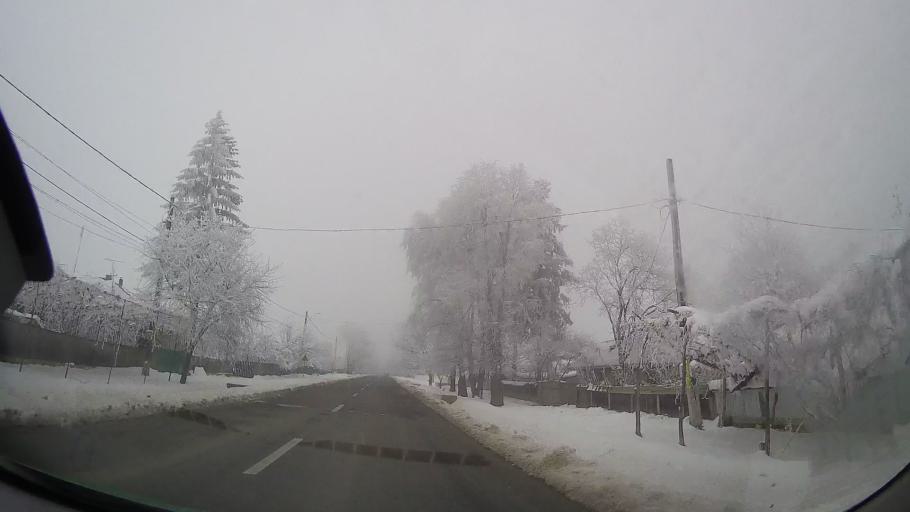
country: RO
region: Iasi
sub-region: Comuna Mogosesti-Siret
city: Mogosesti-Siret
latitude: 47.1587
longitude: 26.7753
